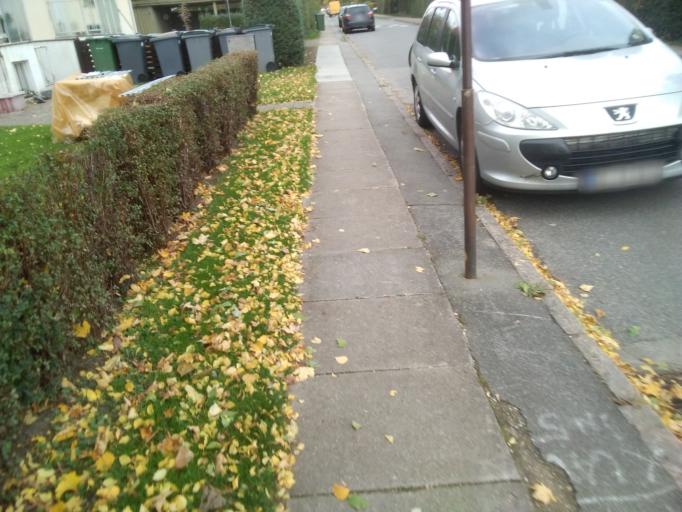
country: DK
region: Capital Region
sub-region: Rodovre Kommune
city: Rodovre
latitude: 55.7060
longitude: 12.4656
